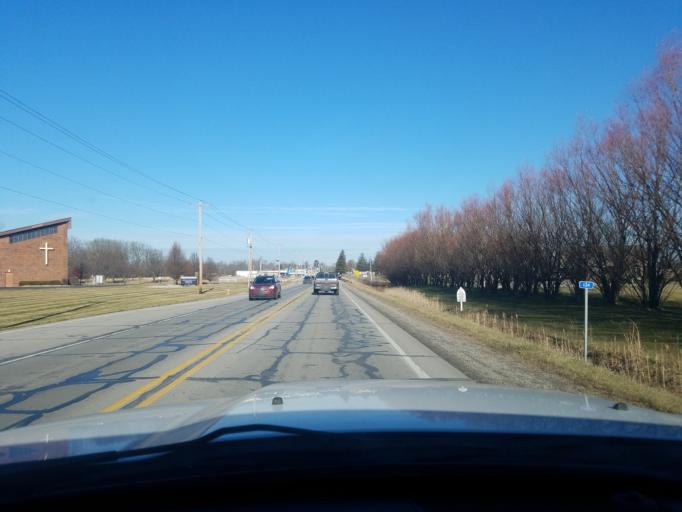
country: US
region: Indiana
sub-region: Wells County
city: Ossian
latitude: 40.8706
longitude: -85.1665
